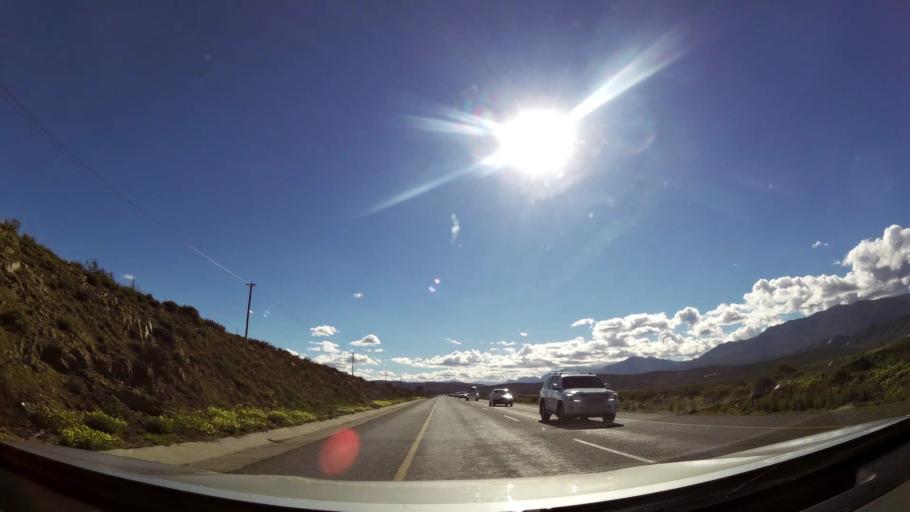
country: ZA
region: Western Cape
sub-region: Cape Winelands District Municipality
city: Worcester
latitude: -33.7590
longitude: 19.7354
